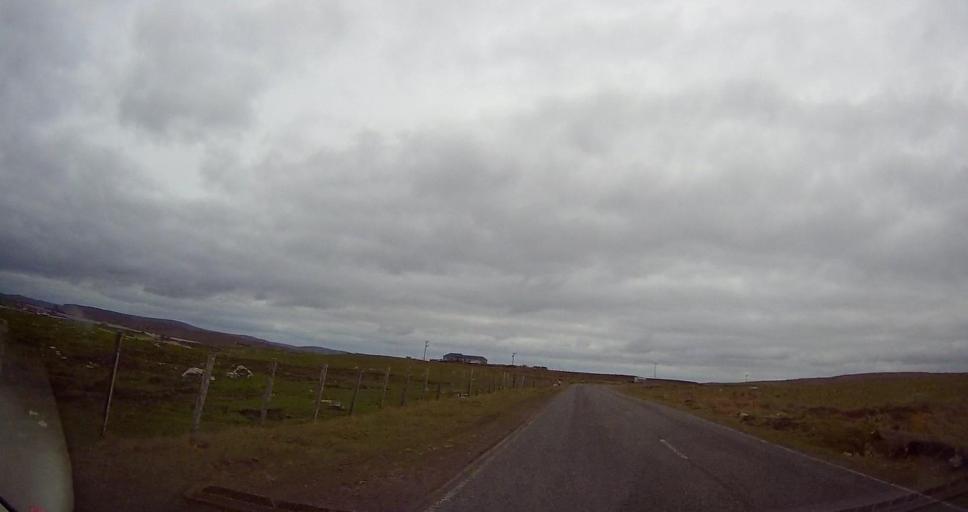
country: GB
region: Scotland
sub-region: Shetland Islands
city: Shetland
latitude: 60.6978
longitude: -0.9219
